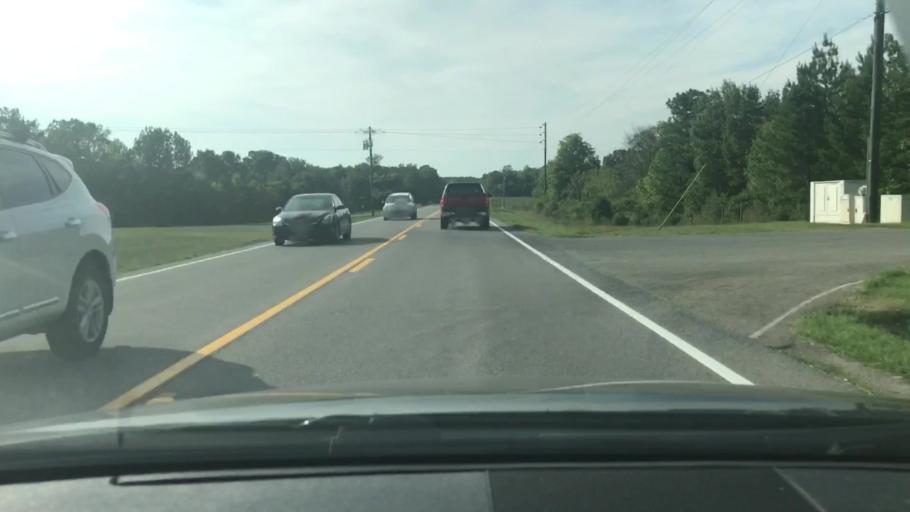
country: US
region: Tennessee
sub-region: Williamson County
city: Fairview
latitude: 36.0200
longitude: -87.1644
